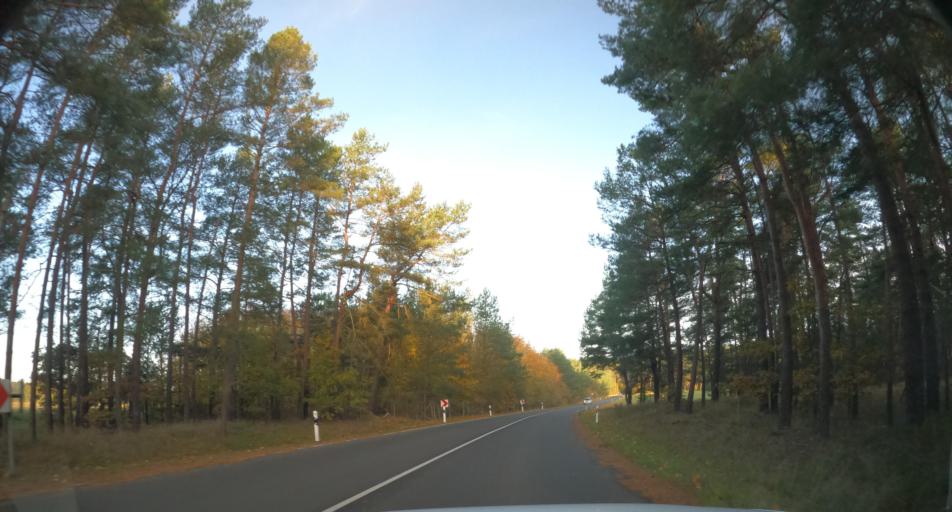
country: DE
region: Mecklenburg-Vorpommern
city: Ahlbeck
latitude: 53.6804
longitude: 14.1762
